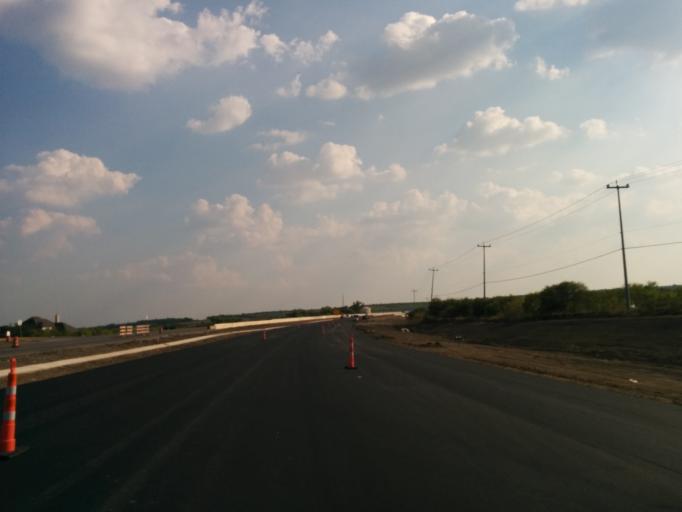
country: US
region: Texas
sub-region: Bexar County
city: Converse
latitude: 29.4891
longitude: -98.2913
